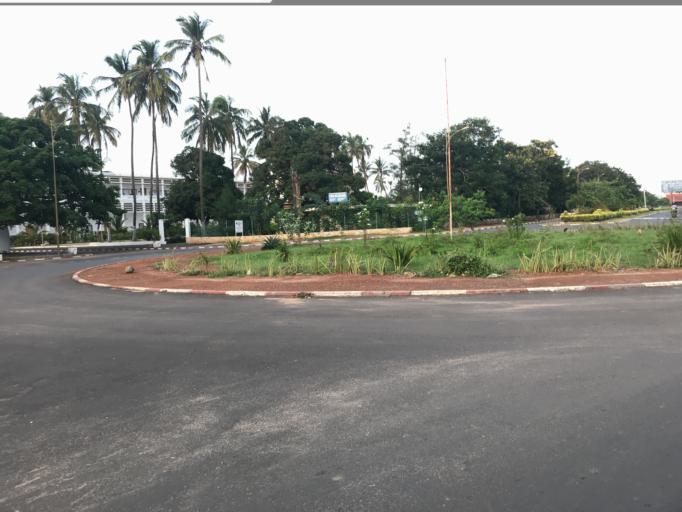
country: SN
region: Dakar
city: Mermoz Boabab
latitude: 14.6854
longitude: -17.4671
